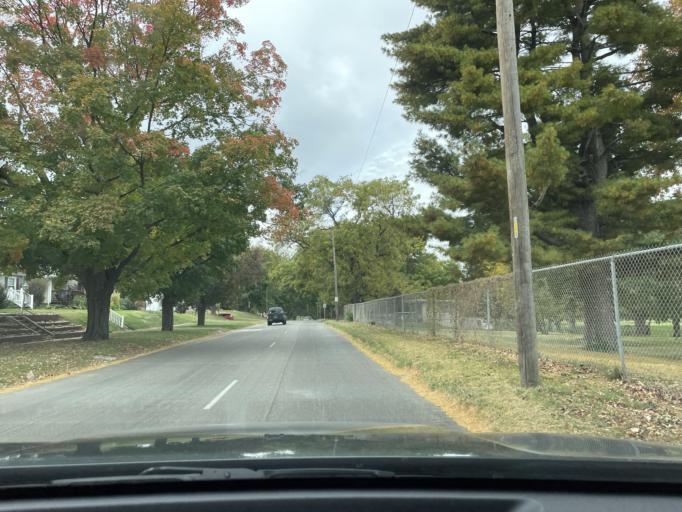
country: US
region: Missouri
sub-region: Buchanan County
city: Saint Joseph
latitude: 39.7693
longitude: -94.8182
